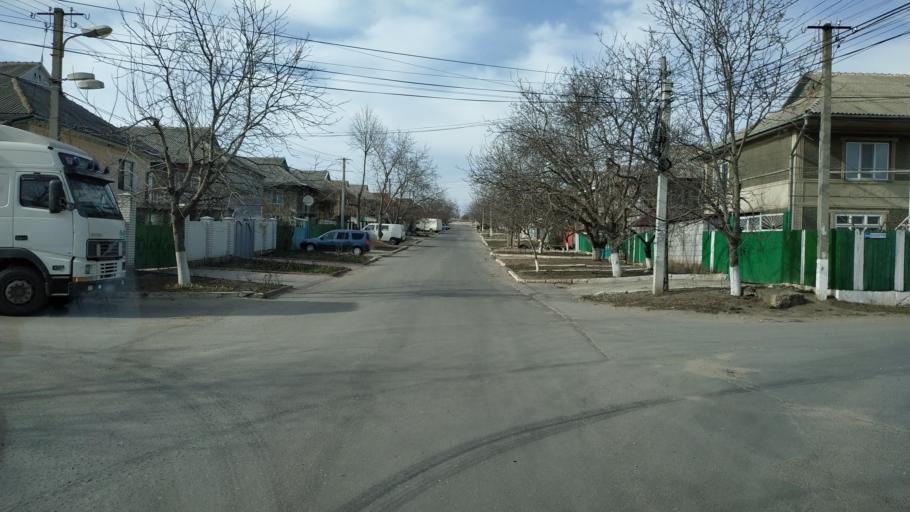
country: MD
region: Chisinau
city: Vatra
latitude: 47.0782
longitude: 28.6891
